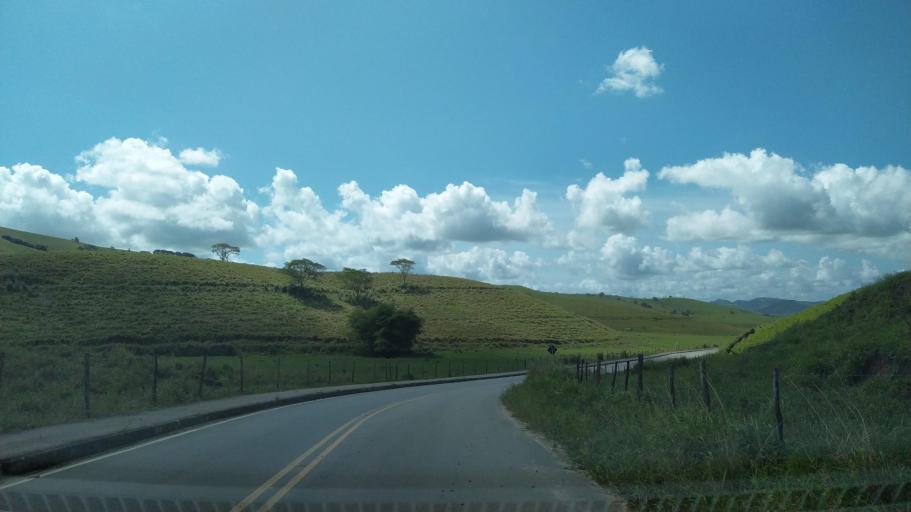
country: BR
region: Alagoas
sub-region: Uniao Dos Palmares
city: Uniao dos Palmares
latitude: -9.1669
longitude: -36.0573
